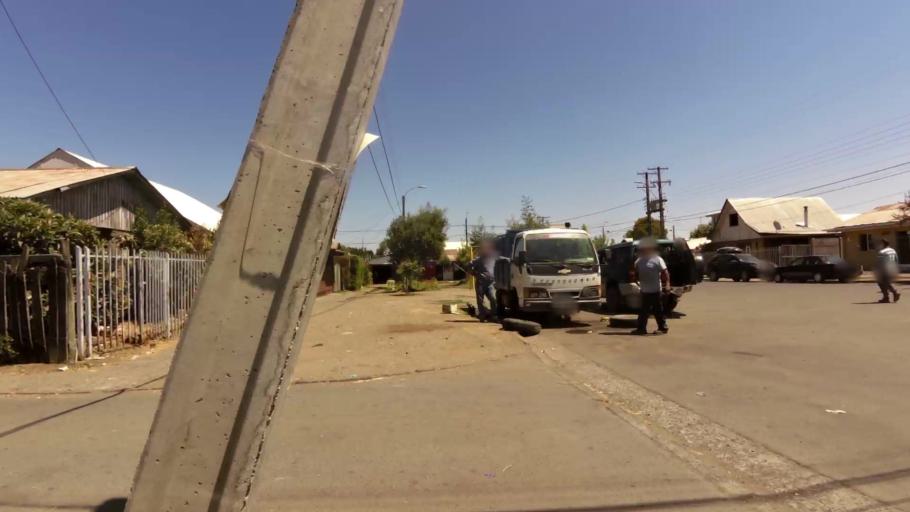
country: CL
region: Maule
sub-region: Provincia de Curico
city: Curico
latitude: -34.9773
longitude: -71.2177
